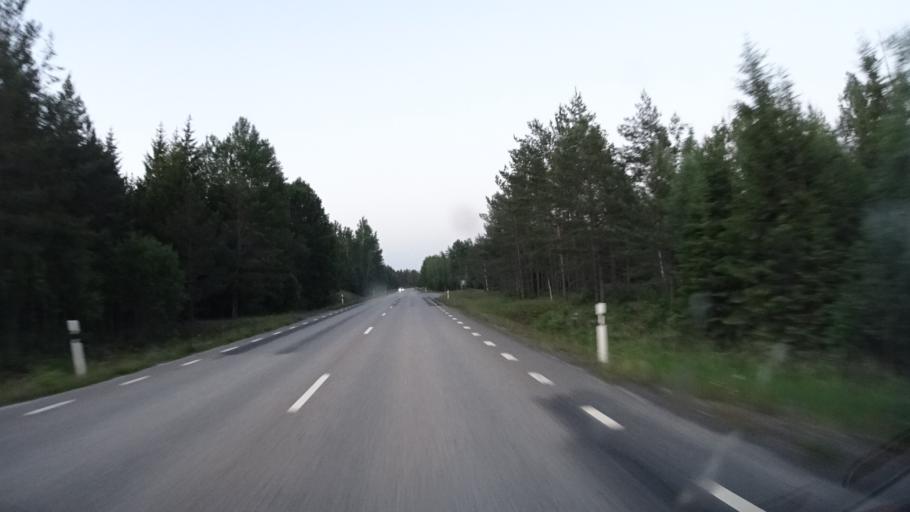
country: SE
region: Kalmar
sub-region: Oskarshamns Kommun
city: Oskarshamn
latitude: 57.2670
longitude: 16.2785
